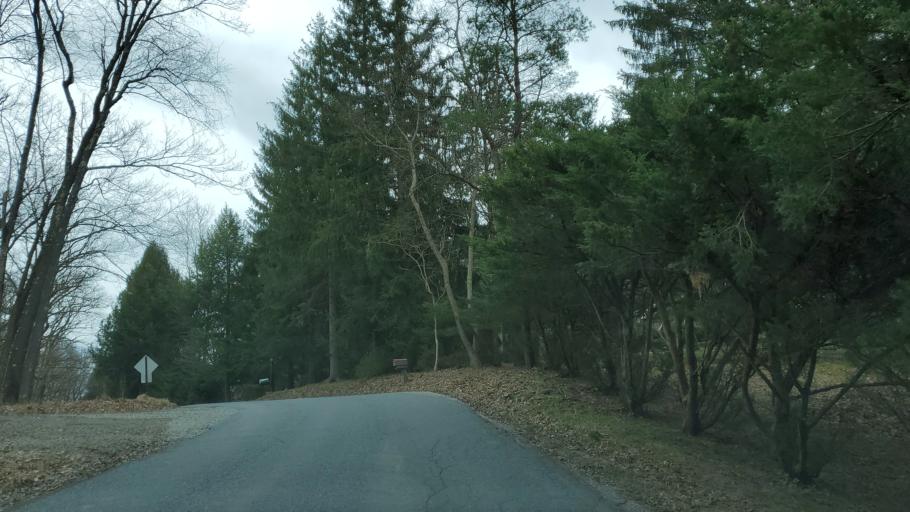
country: US
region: Pennsylvania
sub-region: Westmoreland County
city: Ligonier
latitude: 40.1846
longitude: -79.2457
